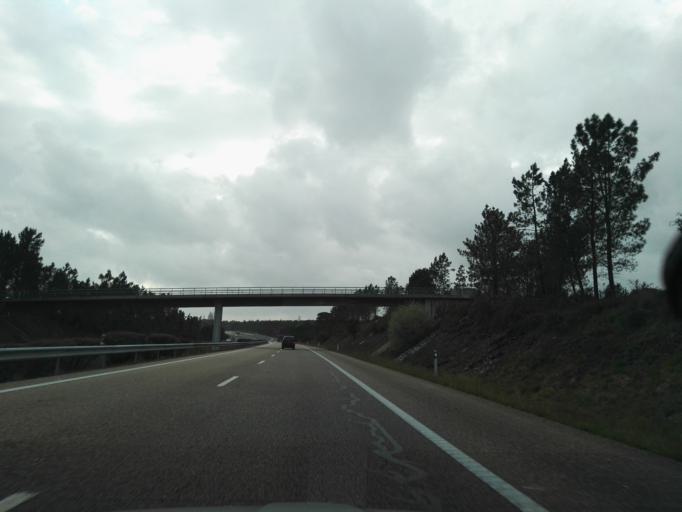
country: PT
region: Evora
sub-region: Vendas Novas
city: Vendas Novas
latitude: 38.6397
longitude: -8.4907
